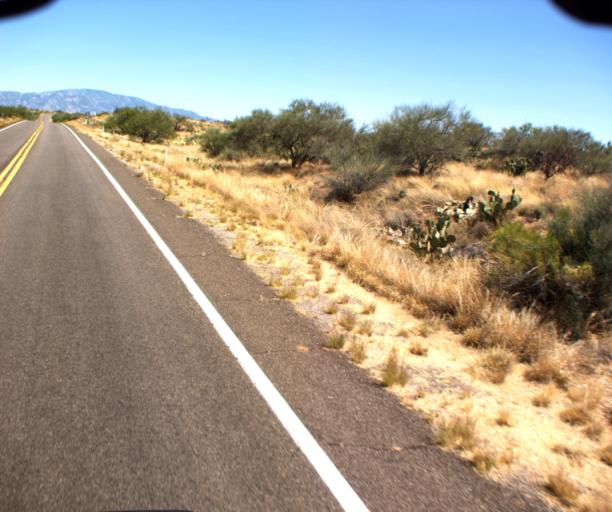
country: US
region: Arizona
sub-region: Pima County
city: Catalina
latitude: 32.6223
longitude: -110.9961
